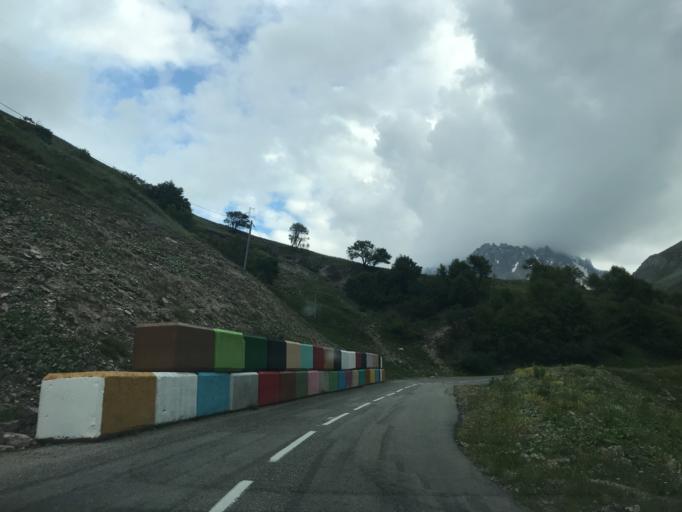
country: FR
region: Rhone-Alpes
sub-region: Departement de la Savoie
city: Valloire
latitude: 45.1016
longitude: 6.4294
